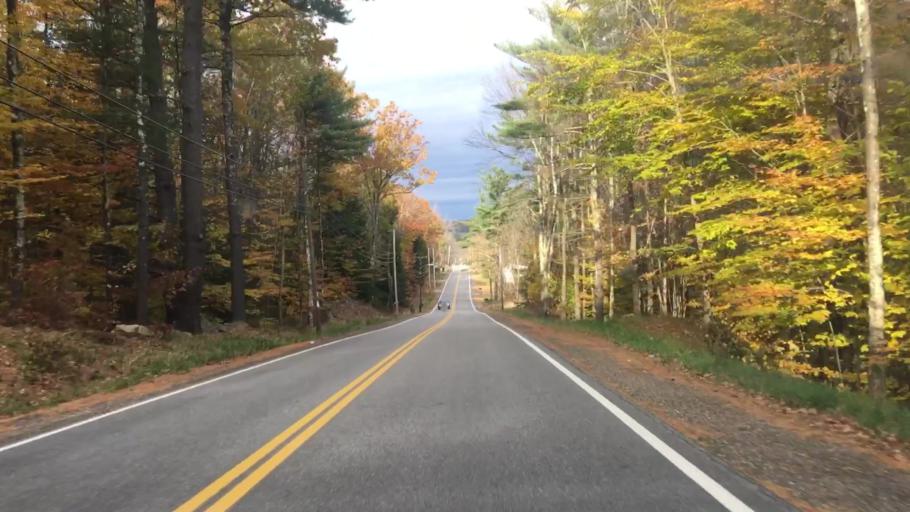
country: US
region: Maine
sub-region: York County
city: Springvale
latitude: 43.4555
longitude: -70.8064
